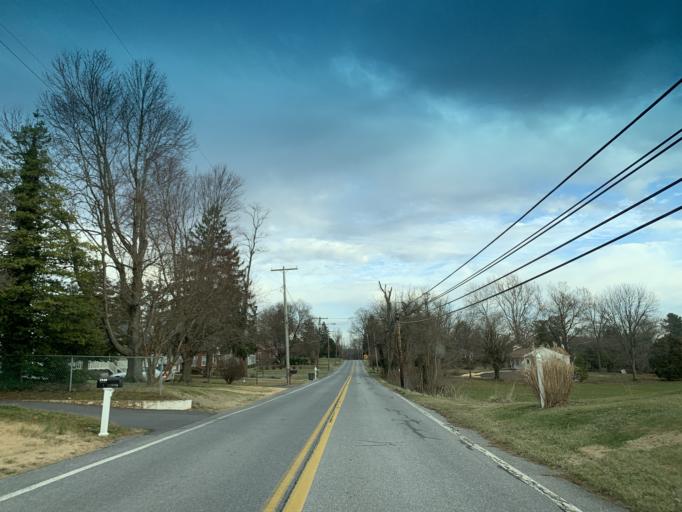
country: US
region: Maryland
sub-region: Frederick County
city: Brunswick
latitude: 39.3304
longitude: -77.6255
